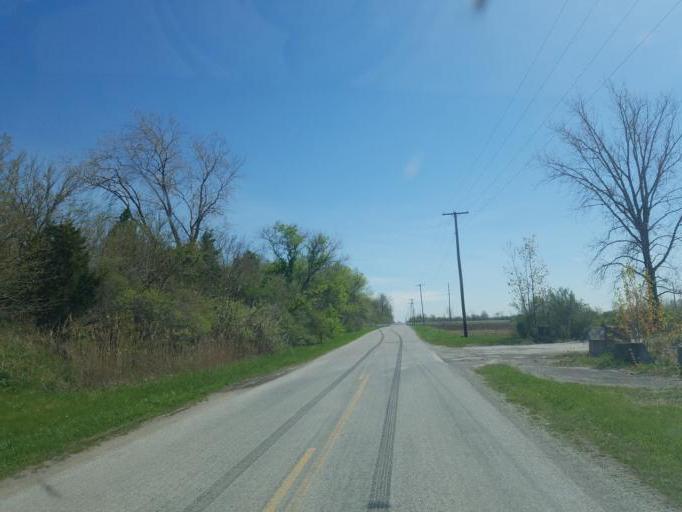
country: US
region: Ohio
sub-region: Huron County
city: Bellevue
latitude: 41.3364
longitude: -82.7937
